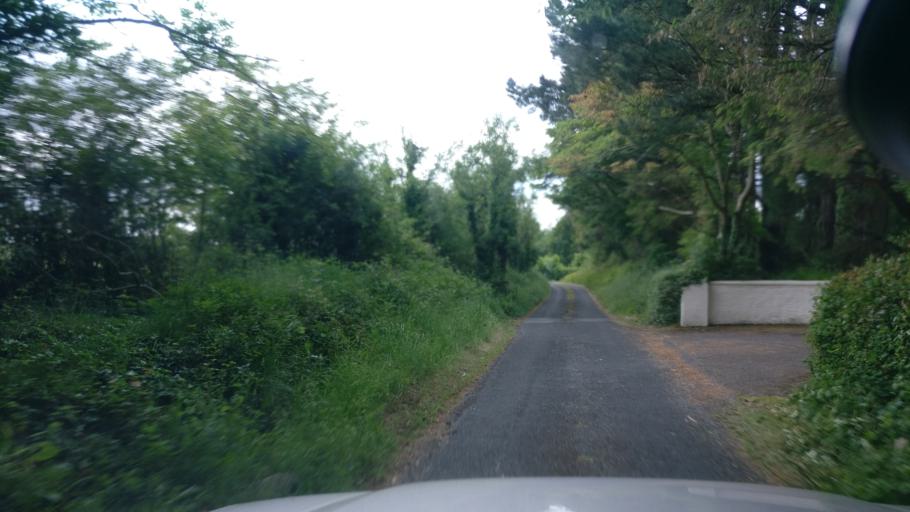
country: IE
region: Connaught
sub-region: County Galway
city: Ballinasloe
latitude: 53.2722
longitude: -8.3629
